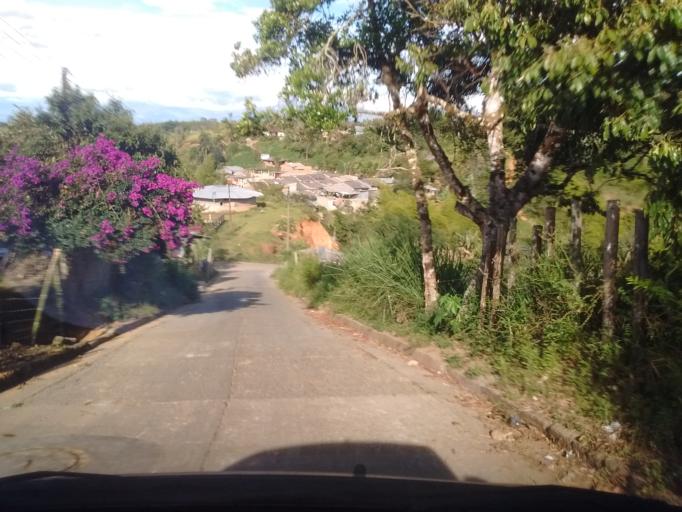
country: CO
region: Cauca
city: El Tambo
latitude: 2.4489
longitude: -76.8126
